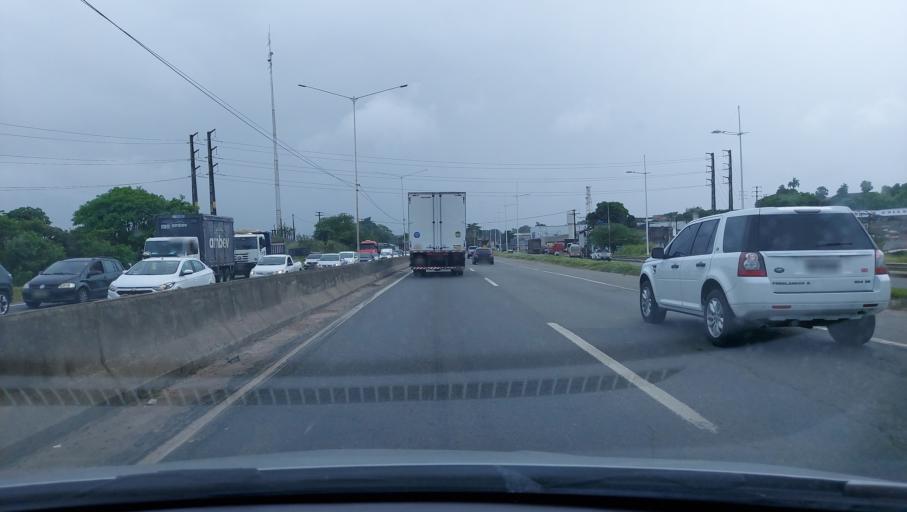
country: BR
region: Bahia
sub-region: Salvador
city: Salvador
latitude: -12.8890
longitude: -38.4426
